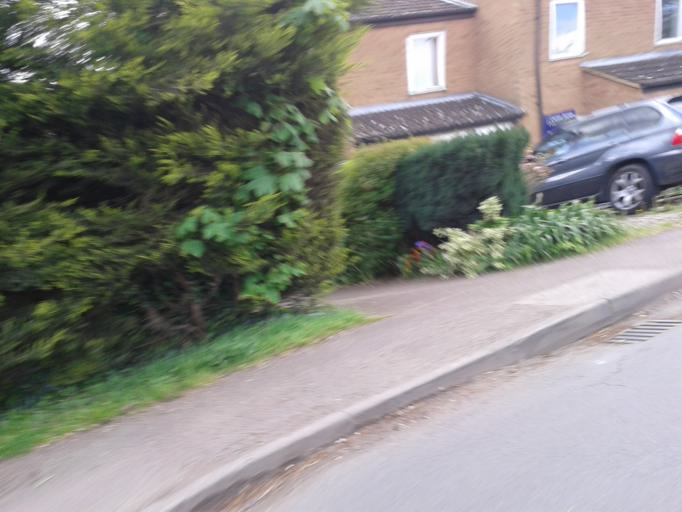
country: GB
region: England
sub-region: Cambridgeshire
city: Cambridge
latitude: 52.2206
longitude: 0.1559
